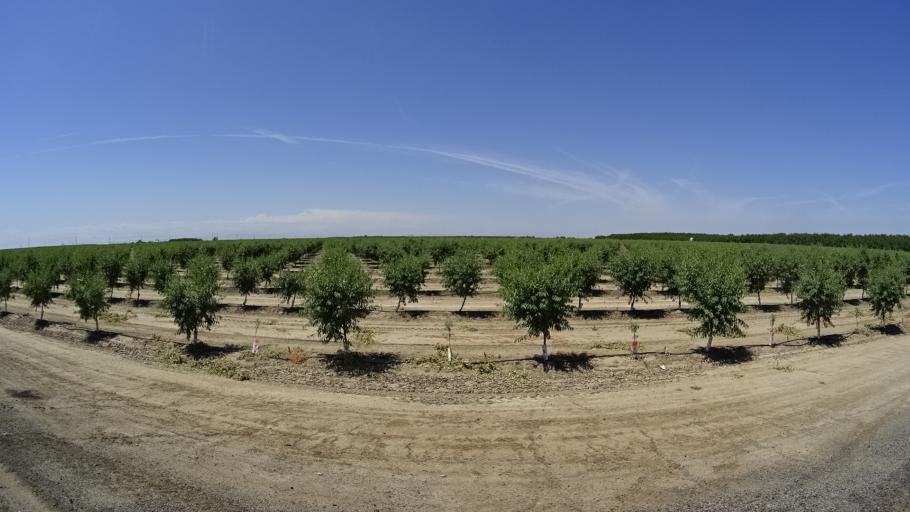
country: US
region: California
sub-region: Kings County
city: Armona
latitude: 36.2456
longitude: -119.6909
